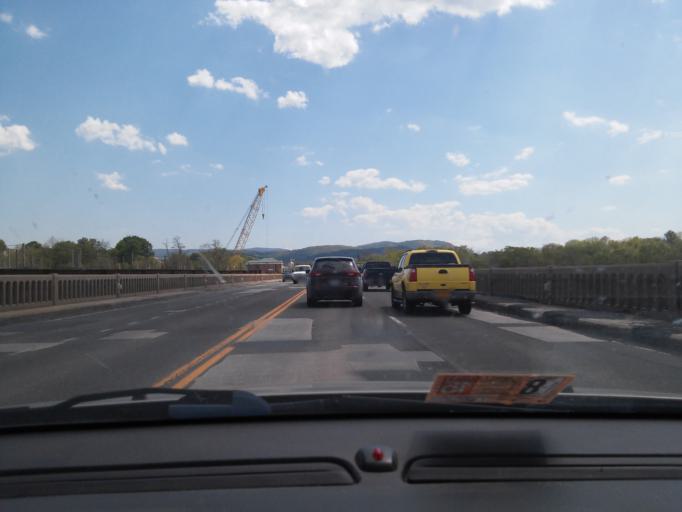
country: US
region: Virginia
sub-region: Warren County
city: Front Royal
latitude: 38.9428
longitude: -78.1995
